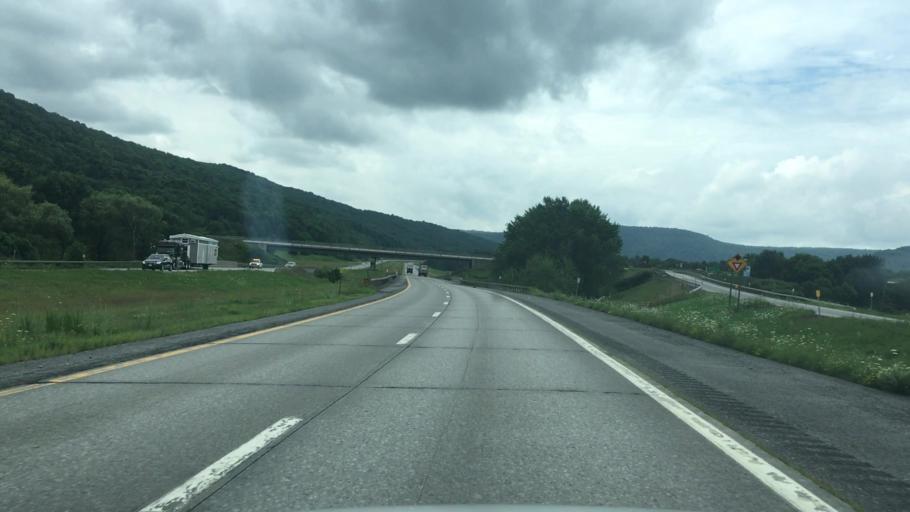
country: US
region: New York
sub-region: Otsego County
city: Worcester
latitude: 42.5936
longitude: -74.7256
